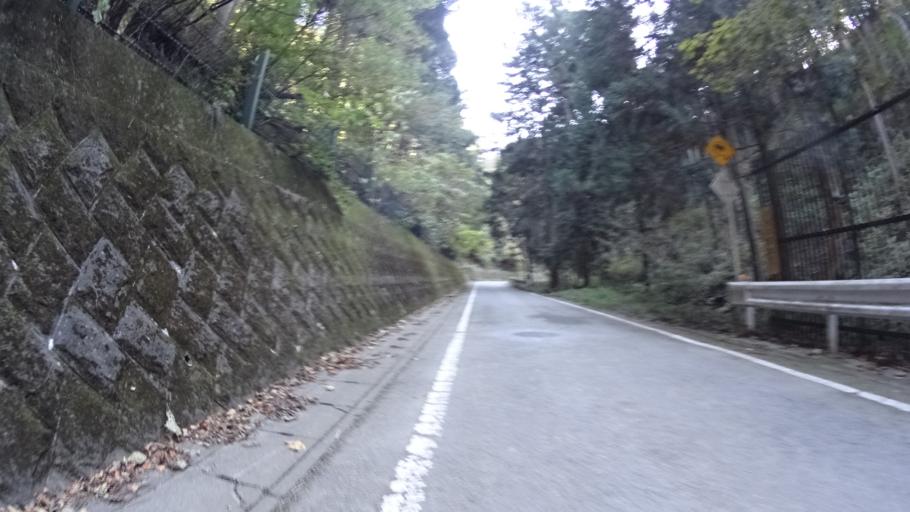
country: JP
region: Yamanashi
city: Uenohara
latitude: 35.6585
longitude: 139.1583
